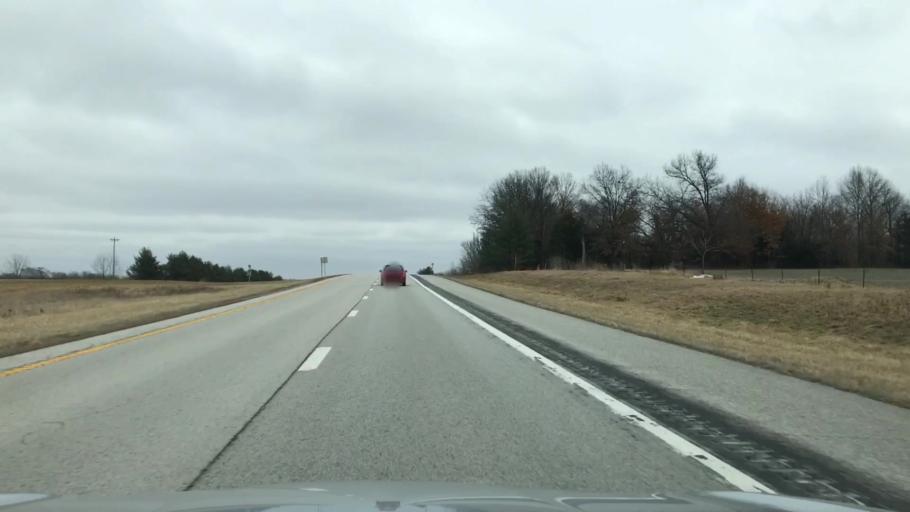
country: US
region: Missouri
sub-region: Livingston County
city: Chillicothe
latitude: 39.7771
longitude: -93.3702
